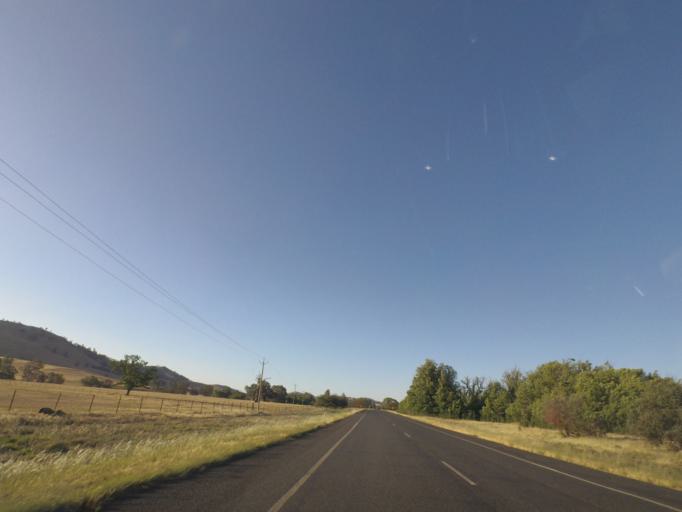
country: AU
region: New South Wales
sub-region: Gundagai
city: Gundagai
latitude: -34.9387
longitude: 148.1678
